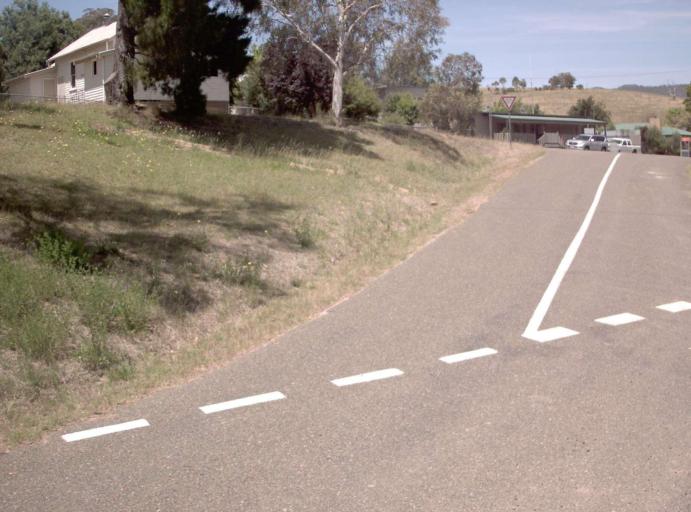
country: AU
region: Victoria
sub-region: East Gippsland
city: Bairnsdale
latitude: -37.3752
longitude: 147.8361
